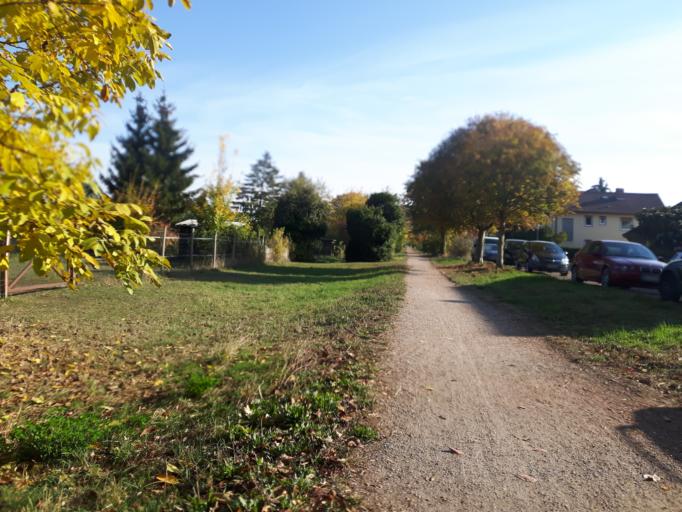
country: DE
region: Rheinland-Pfalz
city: Worms
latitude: 49.6530
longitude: 8.3371
